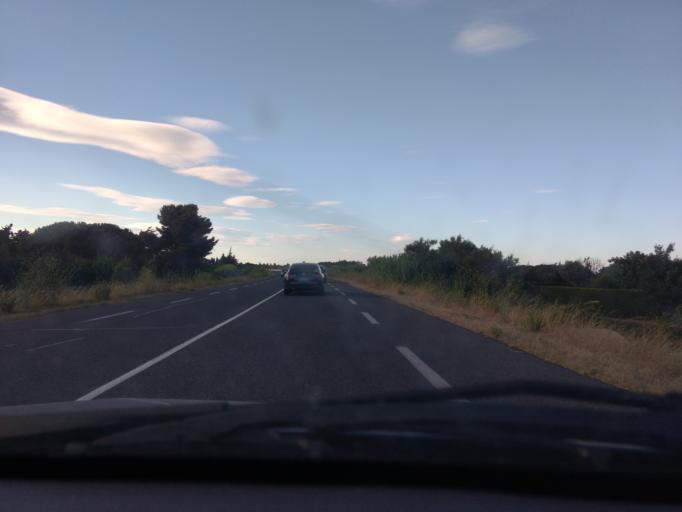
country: FR
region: Languedoc-Roussillon
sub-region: Departement des Pyrenees-Orientales
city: Sainte-Marie-Plage
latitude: 42.7202
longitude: 3.0296
